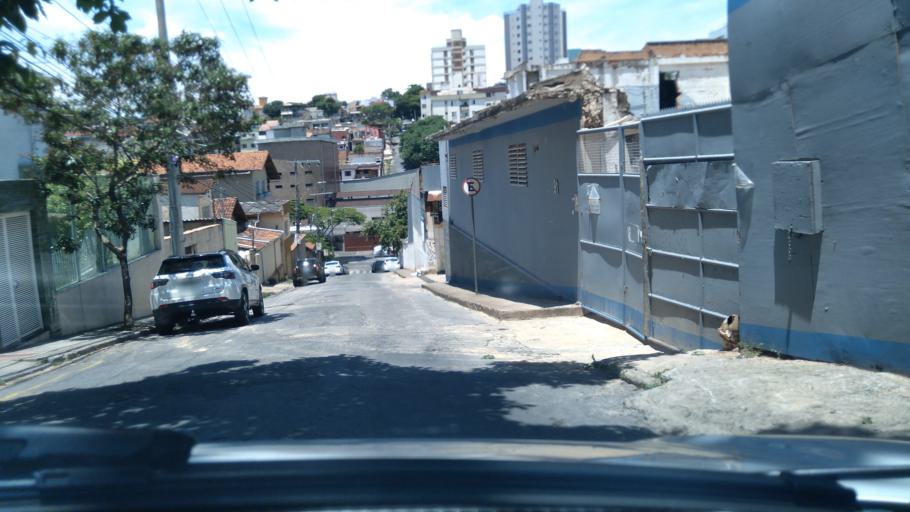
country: BR
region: Minas Gerais
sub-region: Contagem
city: Contagem
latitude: -19.9289
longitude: -43.9961
